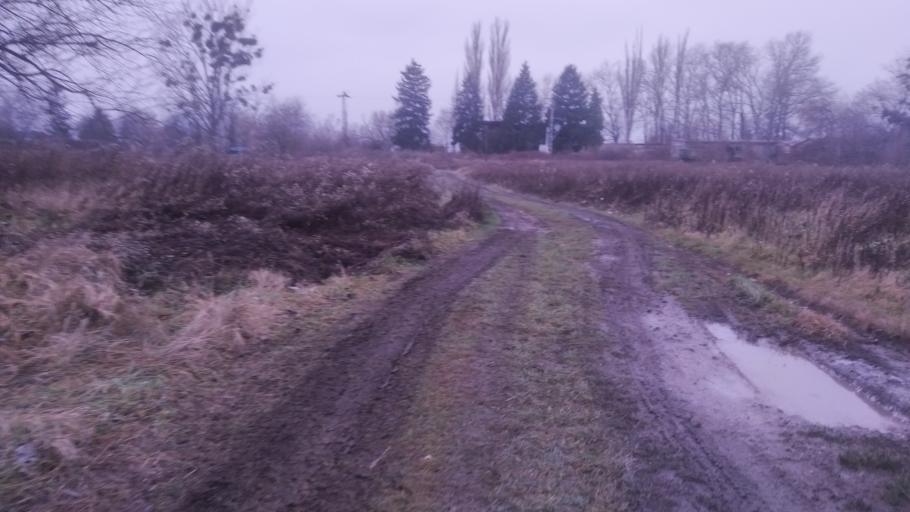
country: HU
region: Komarom-Esztergom
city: Dunaalmas
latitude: 47.7306
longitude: 18.3187
